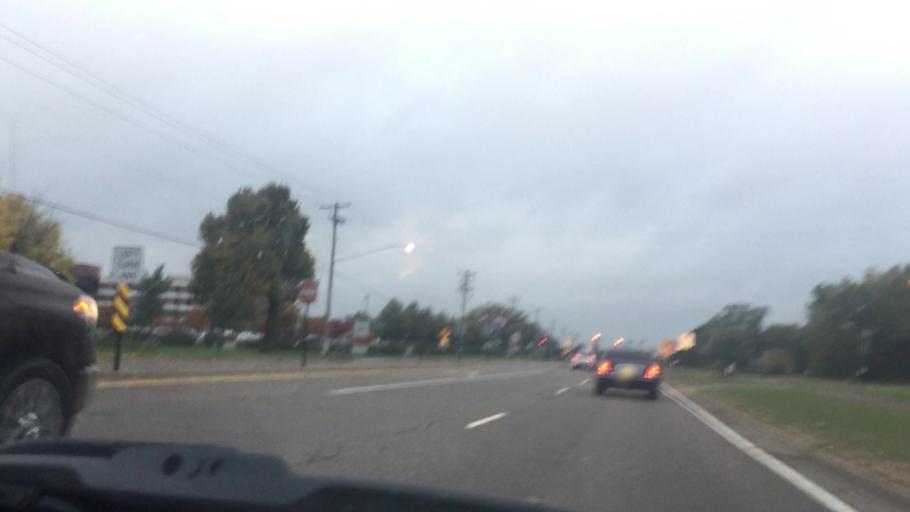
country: US
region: Minnesota
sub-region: Anoka County
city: Spring Lake Park
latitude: 45.1080
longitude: -93.2541
